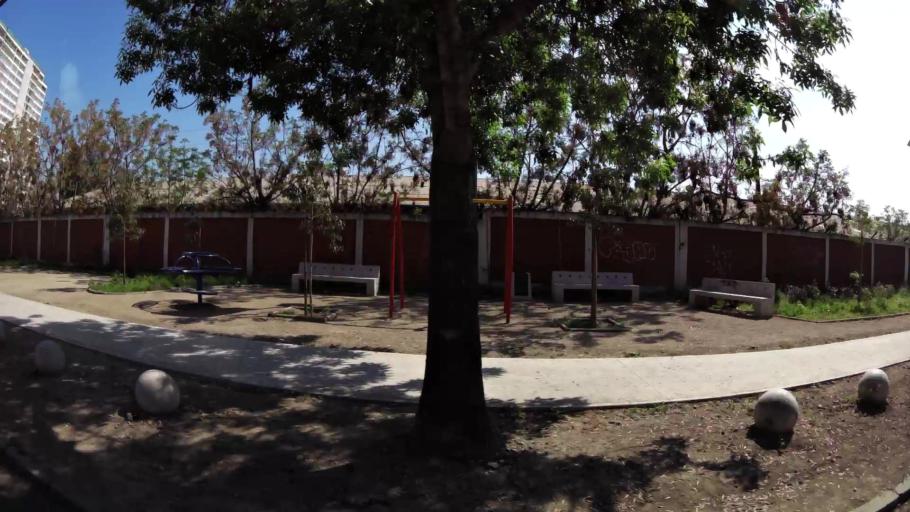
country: CL
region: Santiago Metropolitan
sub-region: Provincia de Santiago
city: Santiago
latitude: -33.4008
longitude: -70.6600
